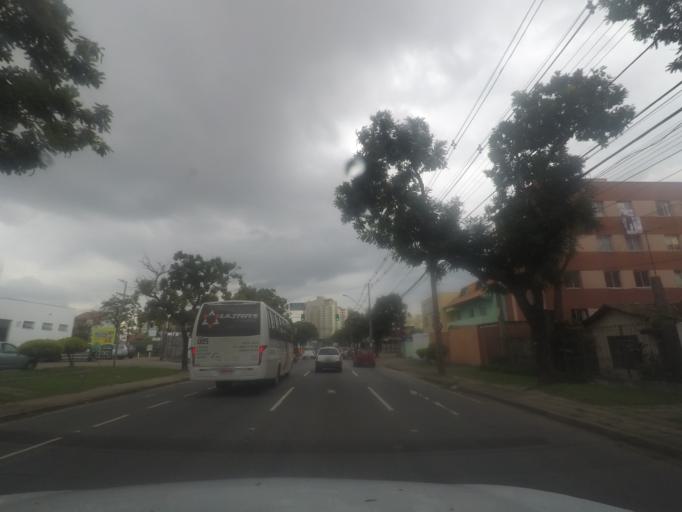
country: BR
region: Parana
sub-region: Curitiba
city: Curitiba
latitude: -25.4920
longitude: -49.2955
